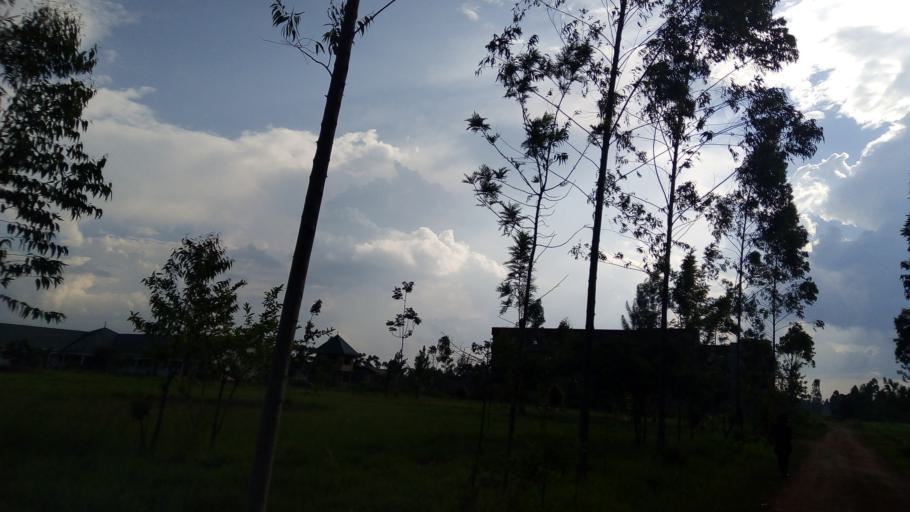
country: UG
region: Eastern Region
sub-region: Mbale District
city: Mbale
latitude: 1.0590
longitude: 34.1694
